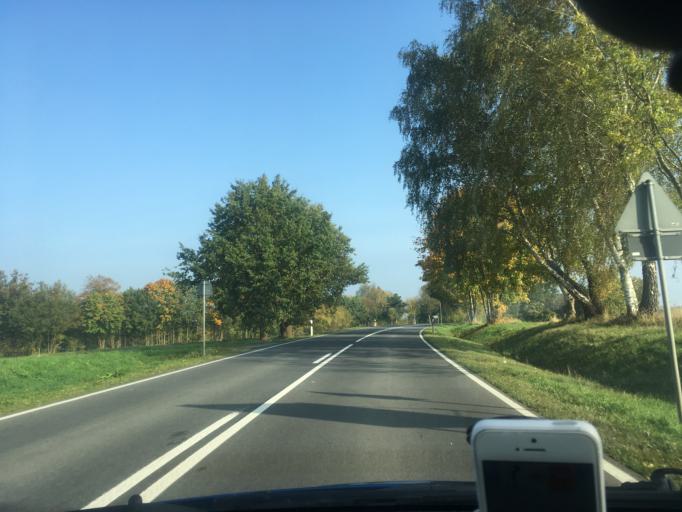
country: DE
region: Mecklenburg-Vorpommern
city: Hagenow
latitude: 53.4339
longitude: 11.1604
